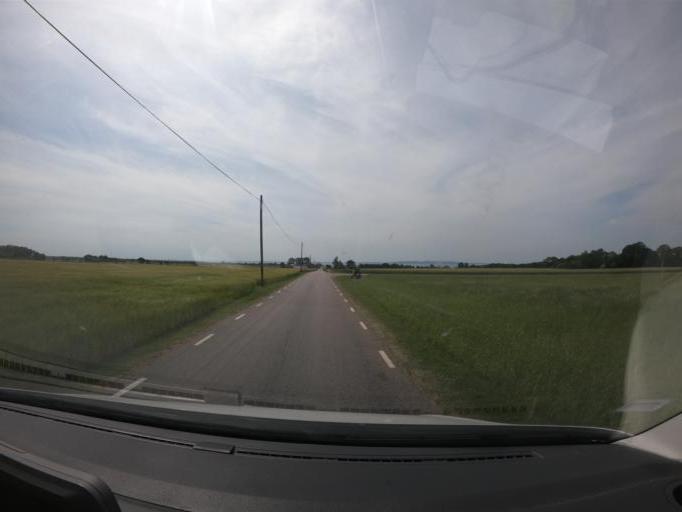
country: SE
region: Skane
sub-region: Angelholms Kommun
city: Vejbystrand
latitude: 56.3734
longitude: 12.7506
